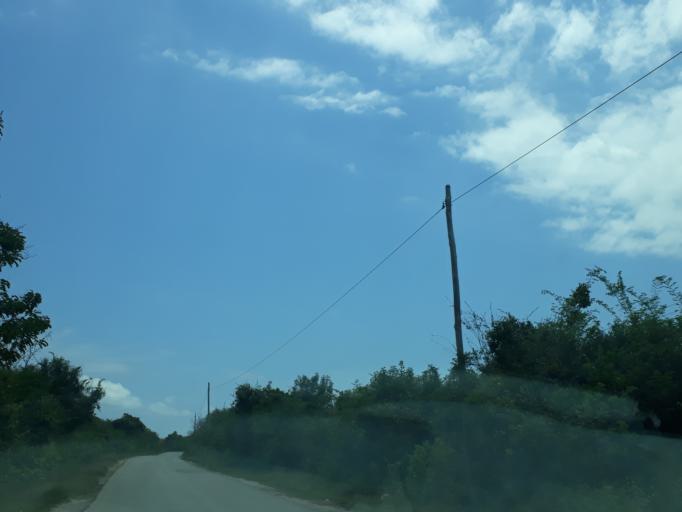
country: TZ
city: Kiwengwa
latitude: -5.9921
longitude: 39.3645
